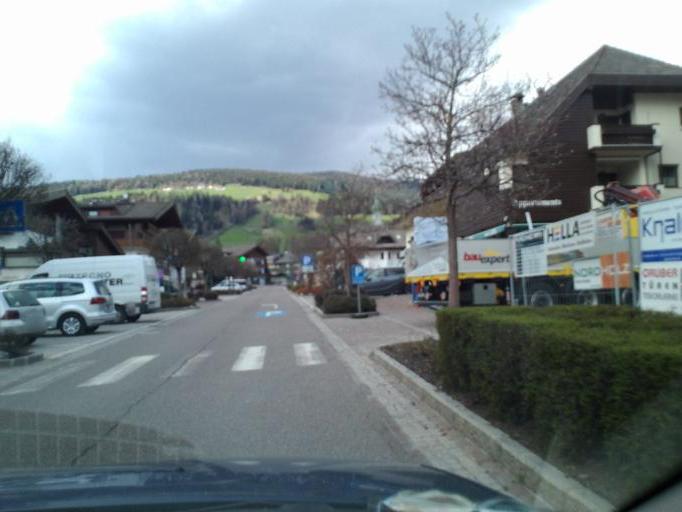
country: IT
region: Trentino-Alto Adige
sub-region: Bolzano
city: Dobbiaco
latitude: 46.7315
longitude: 12.2236
